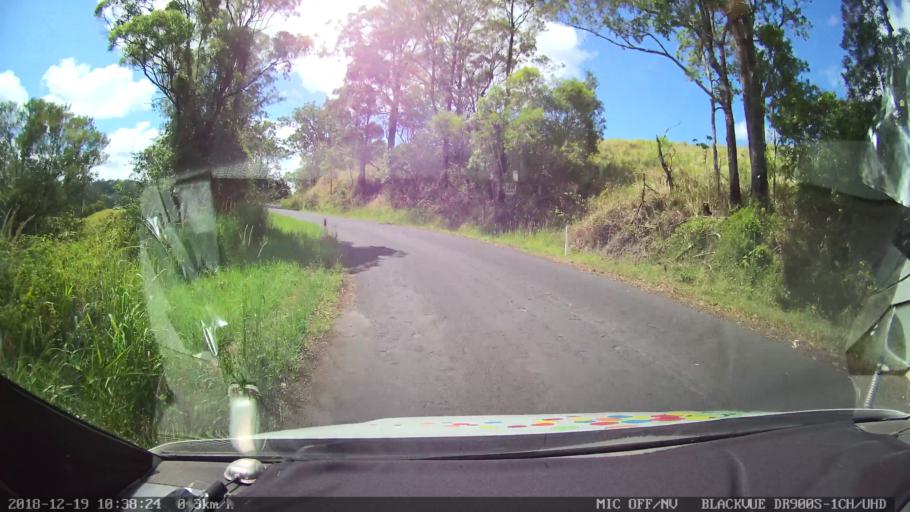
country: AU
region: New South Wales
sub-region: Lismore Municipality
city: Nimbin
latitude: -28.5749
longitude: 153.1543
